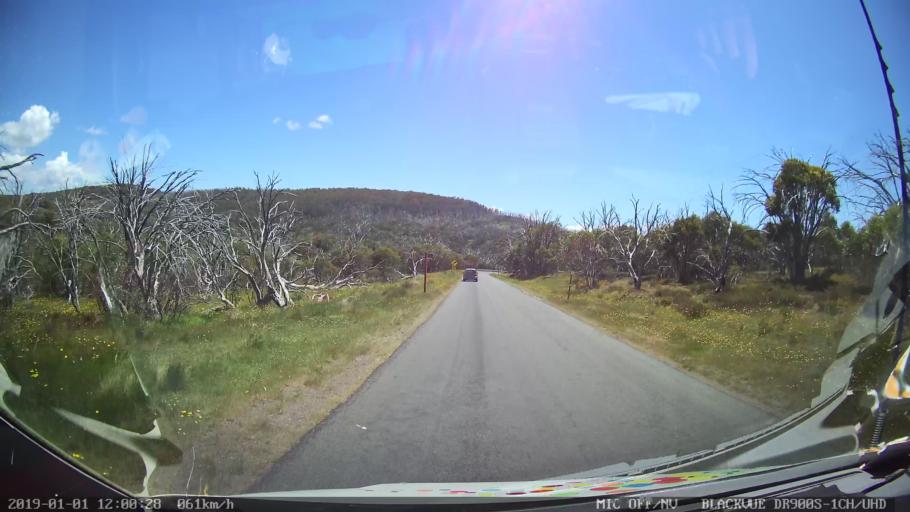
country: AU
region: New South Wales
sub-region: Snowy River
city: Jindabyne
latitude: -35.8846
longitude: 148.4594
